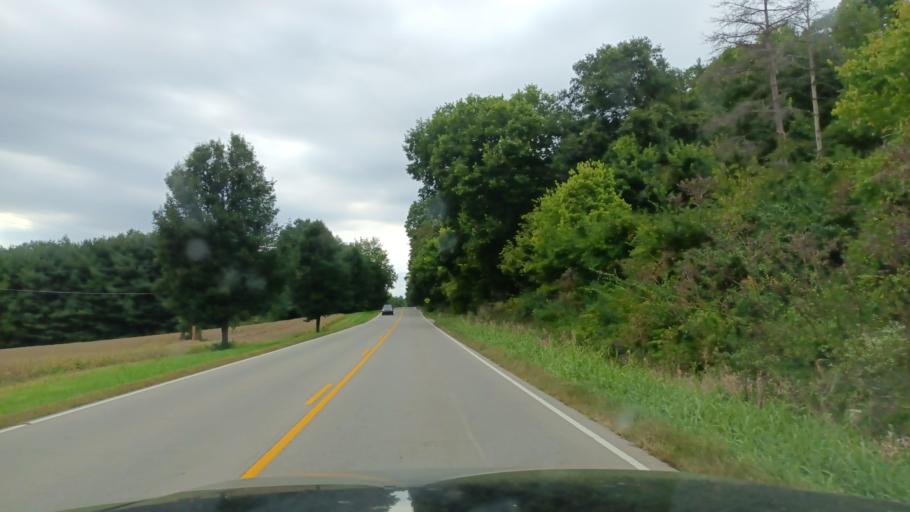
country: US
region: Ohio
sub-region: Ross County
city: Chillicothe
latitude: 39.2833
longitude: -82.8544
